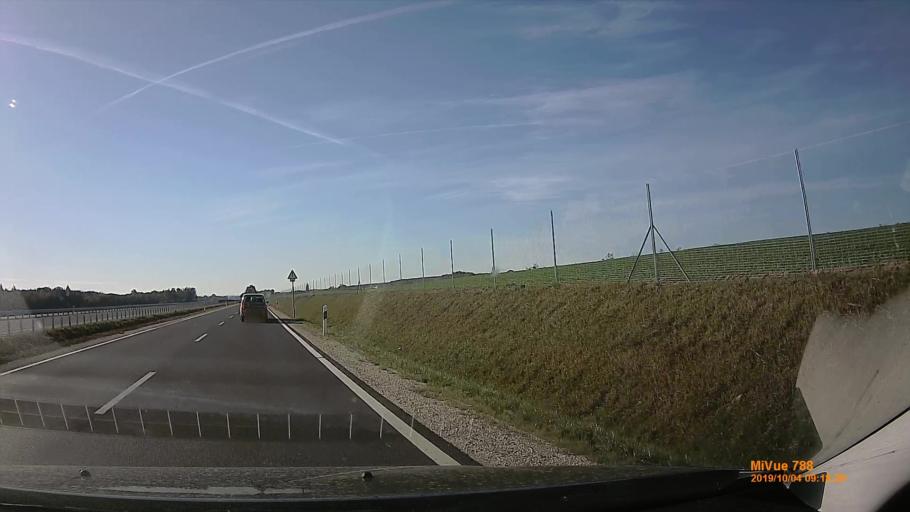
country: HU
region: Somogy
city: Karad
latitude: 46.5903
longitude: 17.8021
